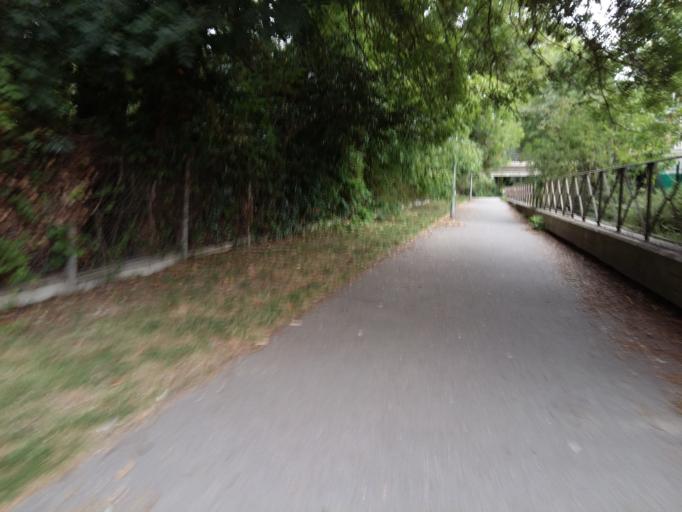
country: FR
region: Picardie
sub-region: Departement de la Somme
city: Amiens
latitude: 49.8973
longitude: 2.2714
